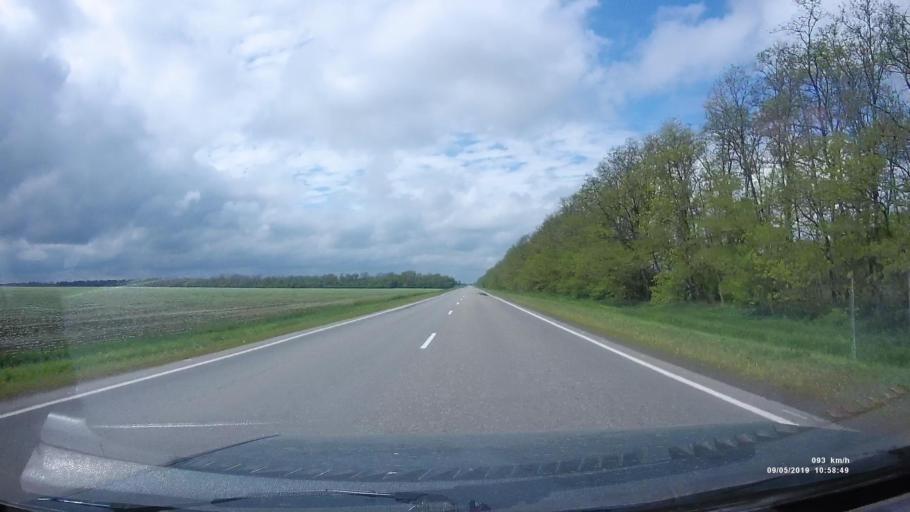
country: RU
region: Rostov
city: Peshkovo
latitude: 46.8603
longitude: 39.2506
